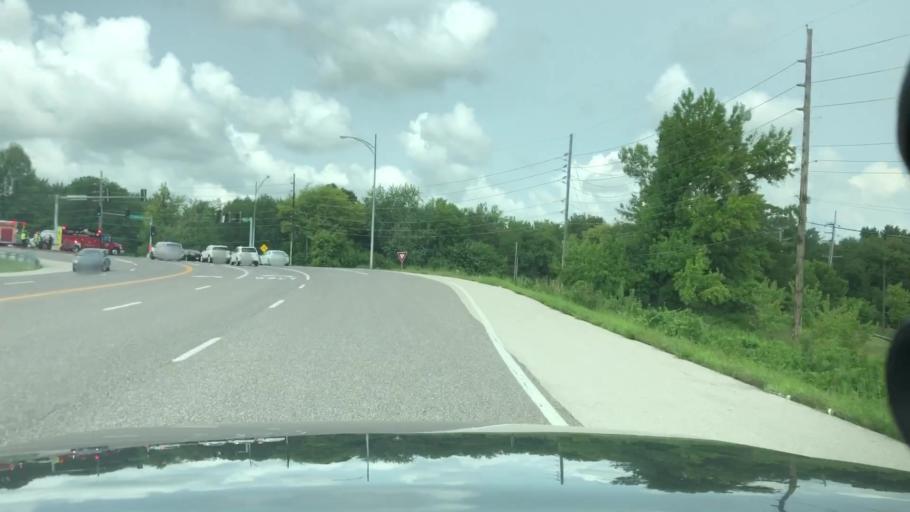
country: US
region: Missouri
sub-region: Saint Charles County
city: Saint Charles
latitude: 38.7878
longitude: -90.5322
